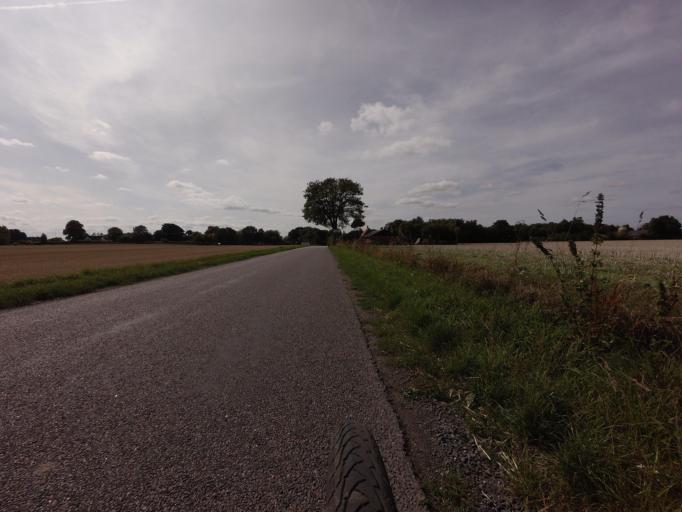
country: DK
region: Zealand
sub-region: Stevns Kommune
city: Store Heddinge
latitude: 55.2430
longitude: 12.3053
